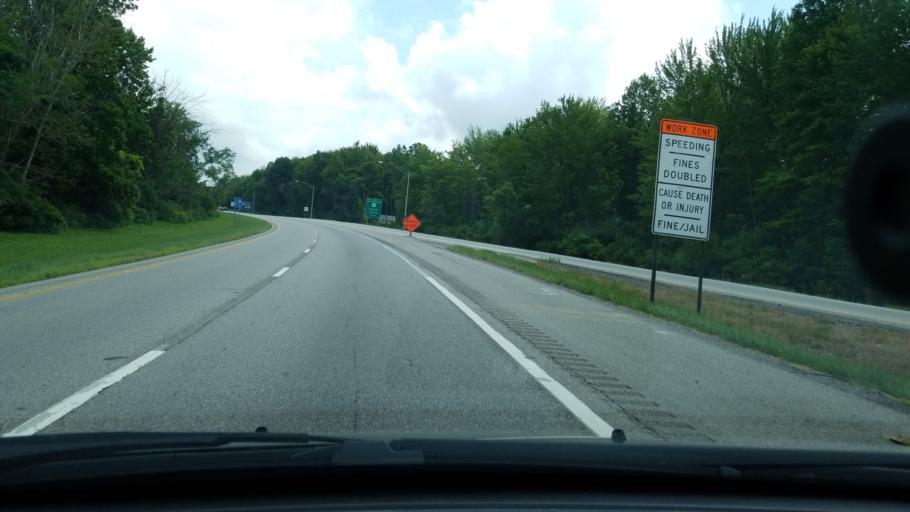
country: US
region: Ohio
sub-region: Lorain County
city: Elyria
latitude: 41.4033
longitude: -82.1428
